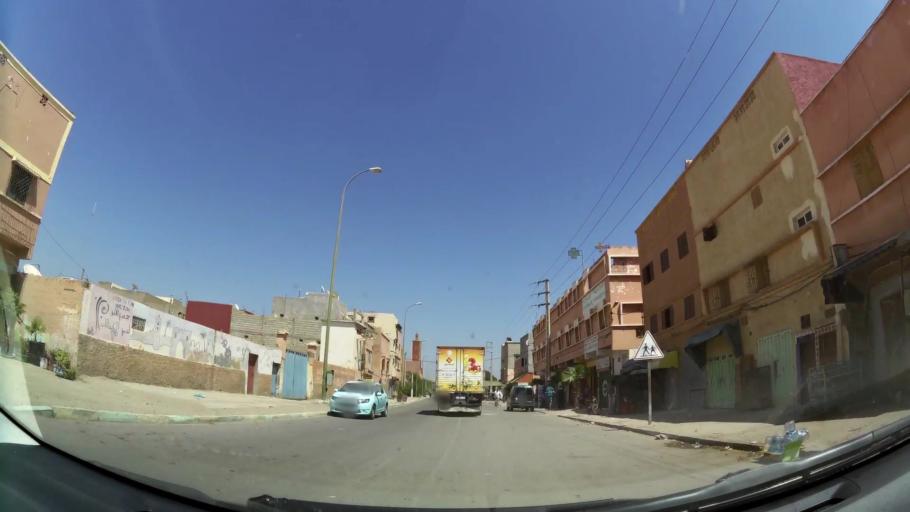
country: MA
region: Souss-Massa-Draa
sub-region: Inezgane-Ait Mellou
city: Inezgane
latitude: 30.3481
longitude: -9.5138
